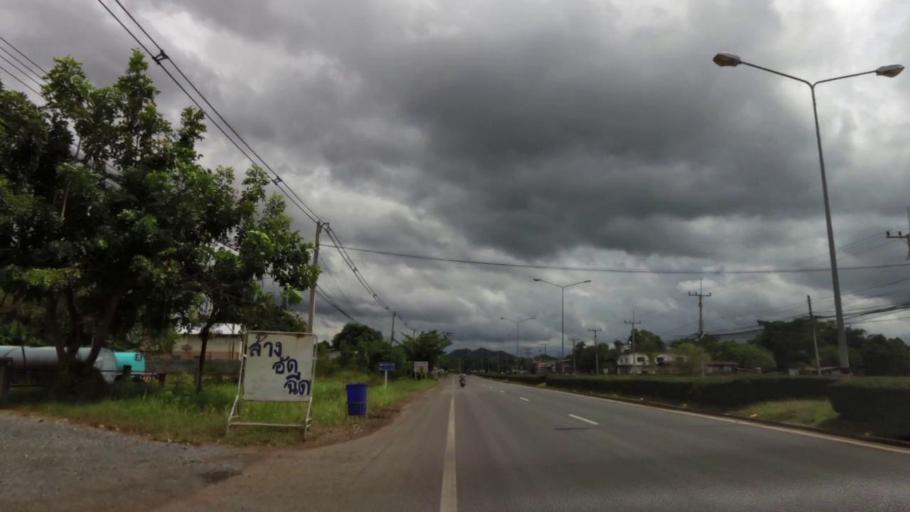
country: TH
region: Nakhon Sawan
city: Phai Sali
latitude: 15.5934
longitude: 100.6538
